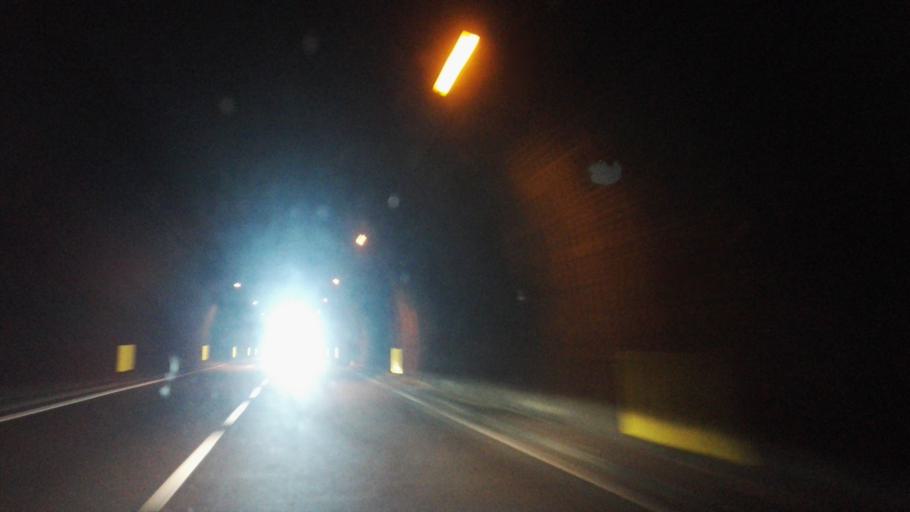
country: IT
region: Calabria
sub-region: Provincia di Catanzaro
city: Marcellinara
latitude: 38.9184
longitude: 16.4765
